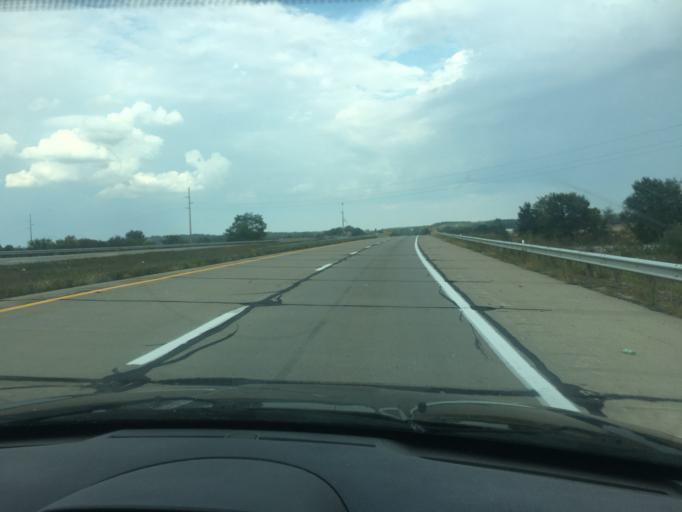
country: US
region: Ohio
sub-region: Clark County
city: Northridge
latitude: 40.0337
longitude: -83.7980
